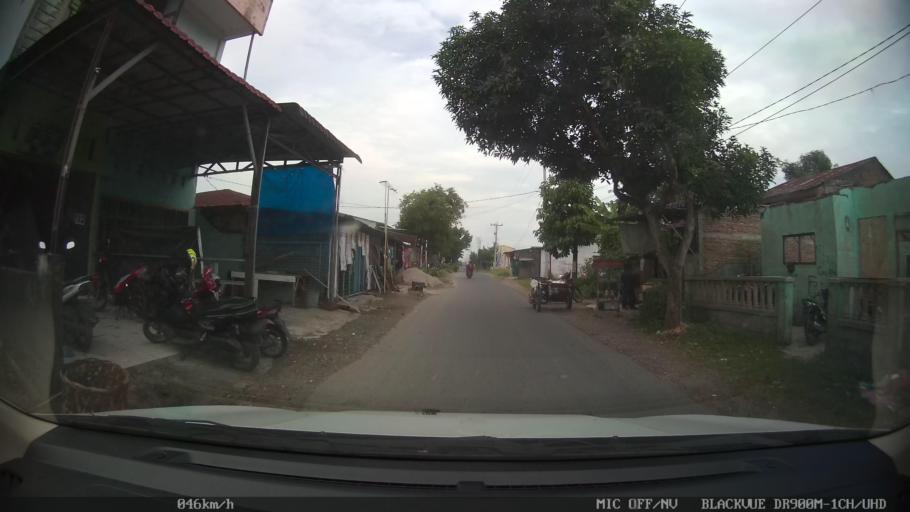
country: ID
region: North Sumatra
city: Sunggal
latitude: 3.6143
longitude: 98.5975
